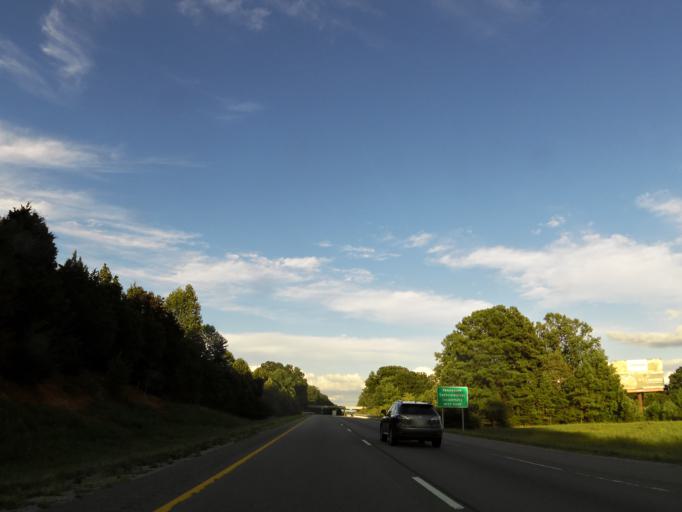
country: US
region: Tennessee
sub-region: Putnam County
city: Cookeville
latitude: 36.1356
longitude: -85.5492
